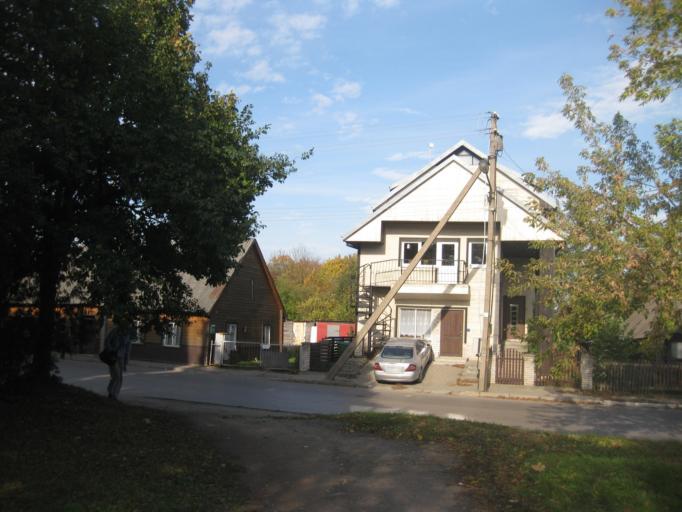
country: LT
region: Kauno apskritis
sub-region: Kaunas
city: Aleksotas
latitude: 54.8866
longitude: 23.8954
